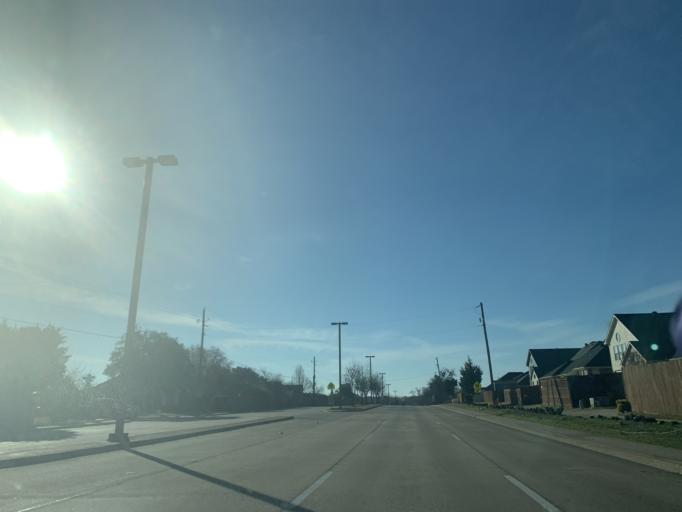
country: US
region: Texas
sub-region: Dallas County
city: DeSoto
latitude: 32.5841
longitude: -96.8399
